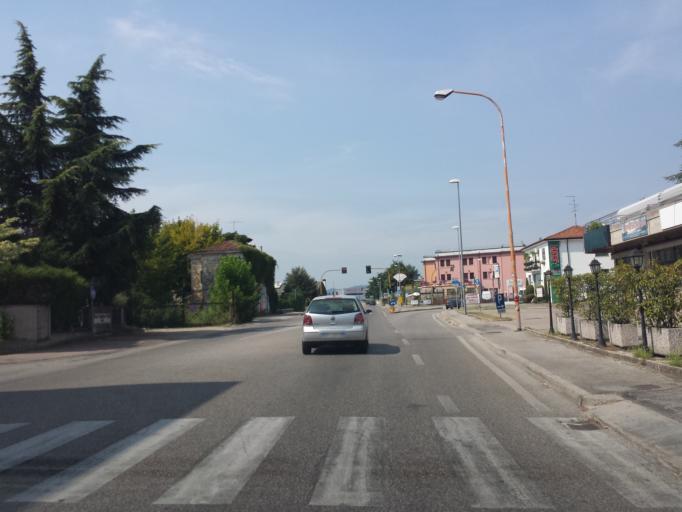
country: IT
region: Veneto
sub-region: Provincia di Vicenza
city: Tavernelle
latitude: 45.5128
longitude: 11.4534
